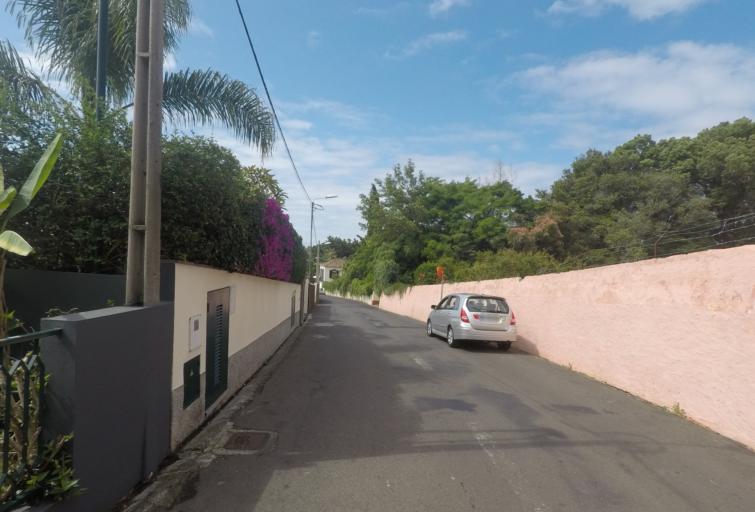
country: PT
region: Madeira
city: Camara de Lobos
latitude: 32.6488
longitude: -16.9351
